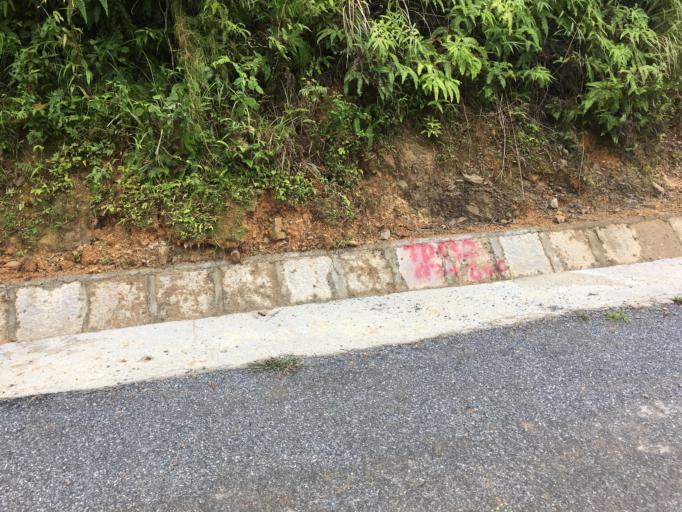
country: VN
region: Ha Giang
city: Thi Tran Tam Son
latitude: 22.9954
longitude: 105.0686
